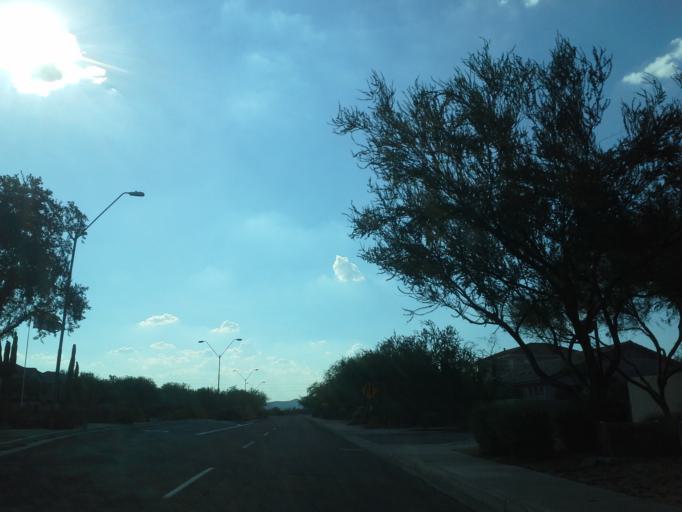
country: US
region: Arizona
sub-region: Maricopa County
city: Cave Creek
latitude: 33.7567
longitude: -111.9927
